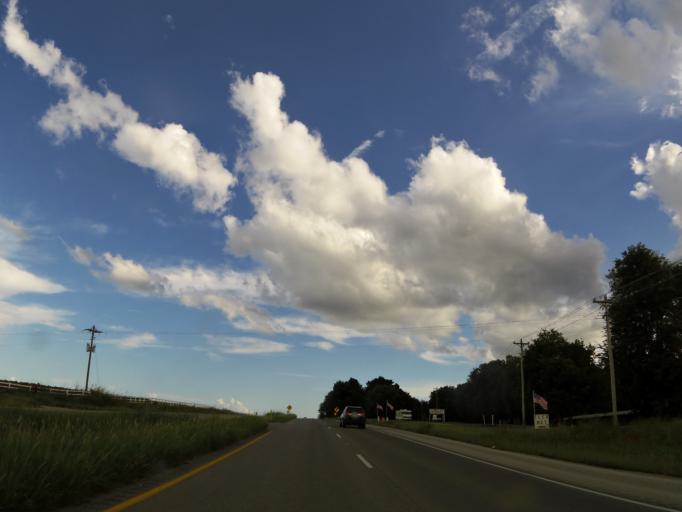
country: US
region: Kentucky
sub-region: Christian County
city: Hopkinsville
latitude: 36.7704
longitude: -87.4719
